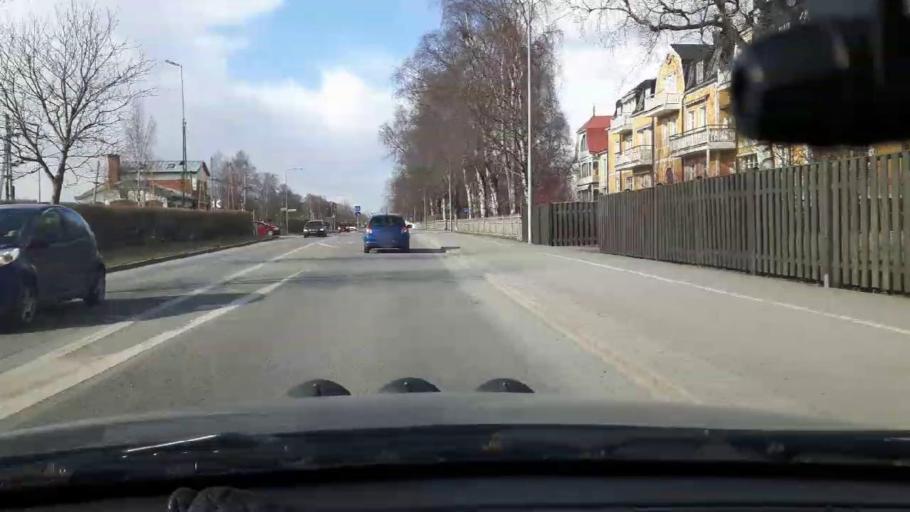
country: SE
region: Jaemtland
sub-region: OEstersunds Kommun
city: Ostersund
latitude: 63.1755
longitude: 14.6321
